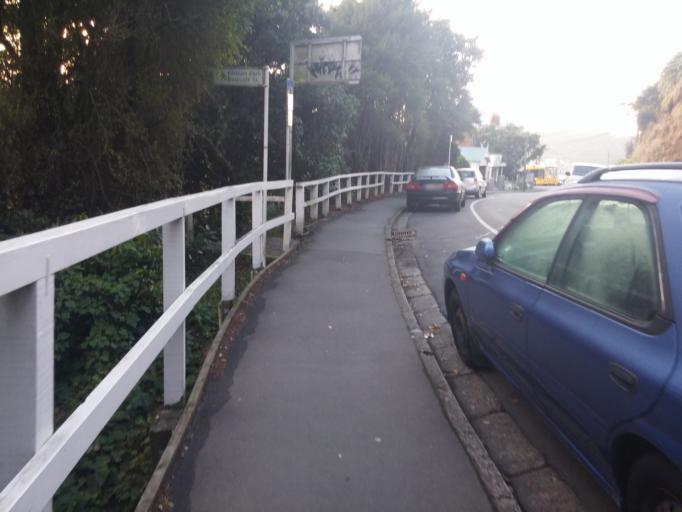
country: NZ
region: Wellington
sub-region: Wellington City
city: Wellington
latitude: -41.2884
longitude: 174.7703
